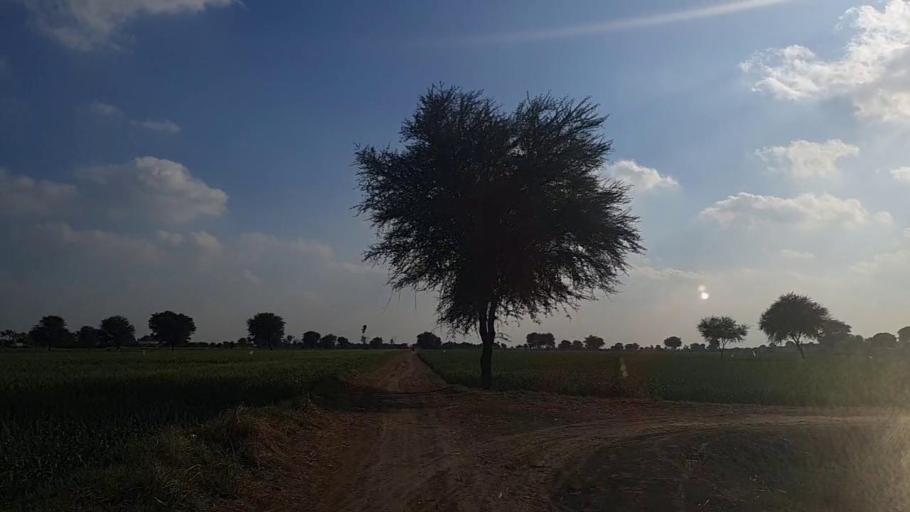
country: PK
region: Sindh
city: Tando Mittha Khan
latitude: 25.9408
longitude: 69.2107
